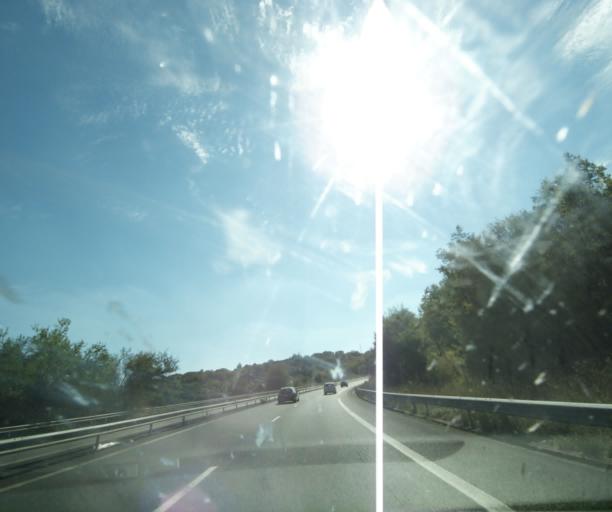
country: FR
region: Limousin
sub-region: Departement de la Correze
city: Brive-la-Gaillarde
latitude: 45.0882
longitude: 1.5191
